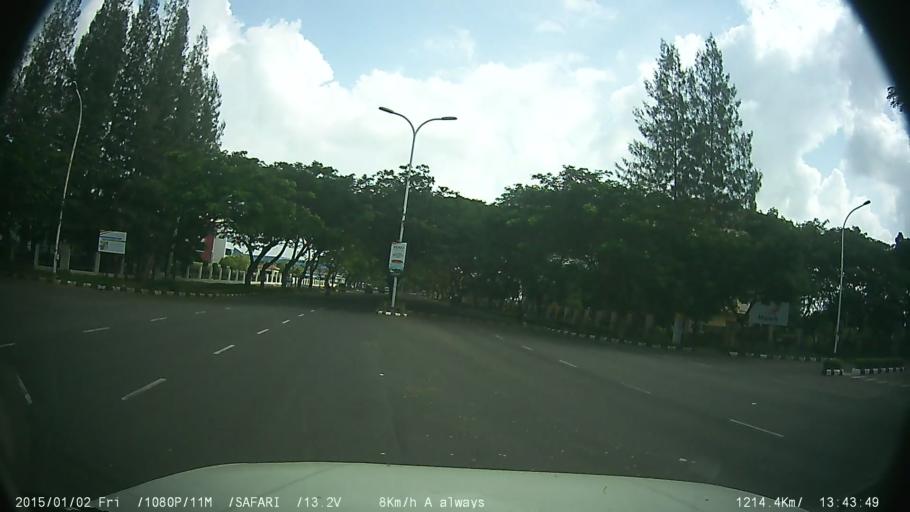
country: IN
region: Tamil Nadu
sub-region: Kancheepuram
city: Singapperumalkovil
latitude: 12.7342
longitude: 80.0109
